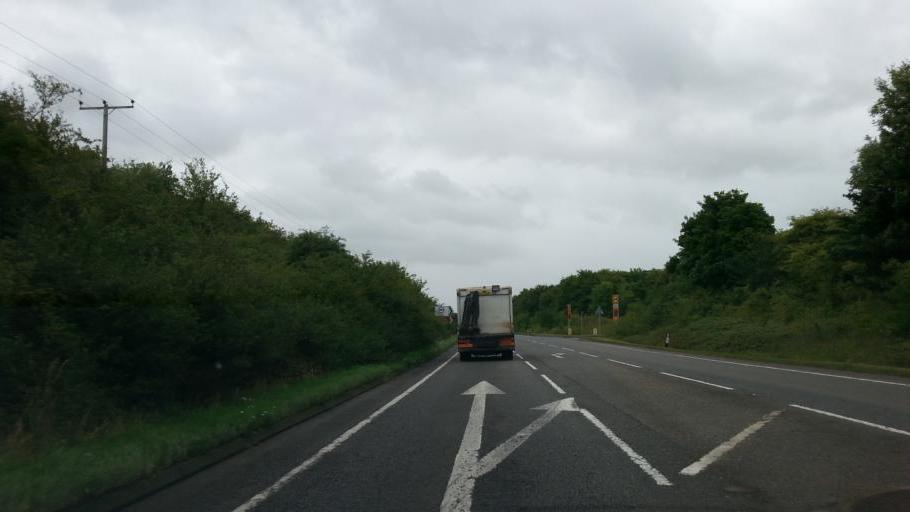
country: GB
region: England
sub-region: Northamptonshire
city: Oundle
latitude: 52.4571
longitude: -0.4626
